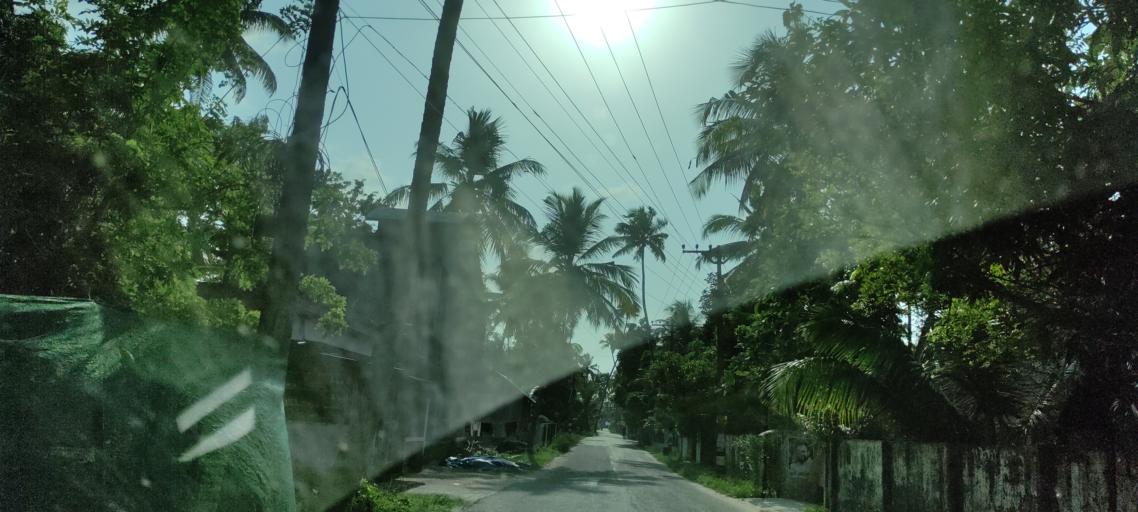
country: IN
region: Kerala
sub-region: Alappuzha
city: Vayalar
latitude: 9.6858
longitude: 76.2941
